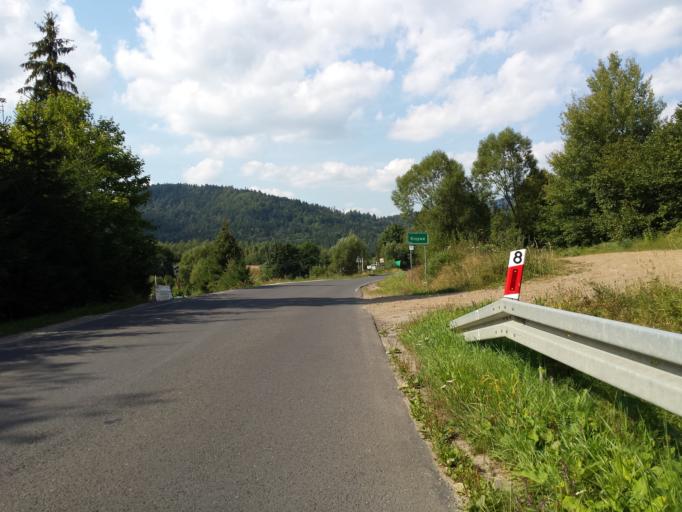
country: PL
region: Subcarpathian Voivodeship
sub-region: Powiat leski
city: Cisna
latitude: 49.1958
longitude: 22.3698
